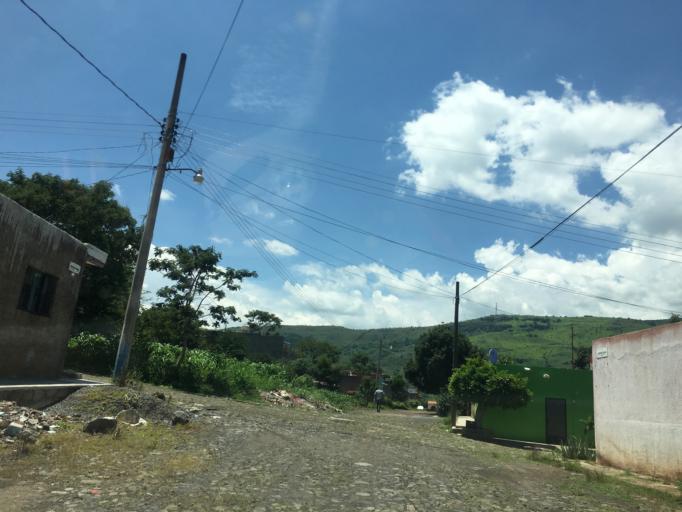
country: MX
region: Nayarit
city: Ixtlan del Rio
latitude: 21.0371
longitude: -104.3510
